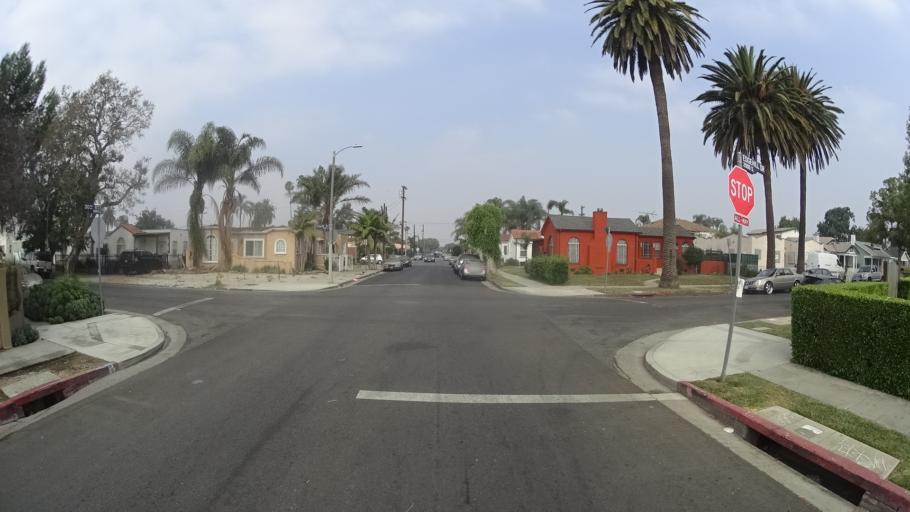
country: US
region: California
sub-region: Los Angeles County
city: View Park-Windsor Hills
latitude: 34.0276
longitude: -118.3303
